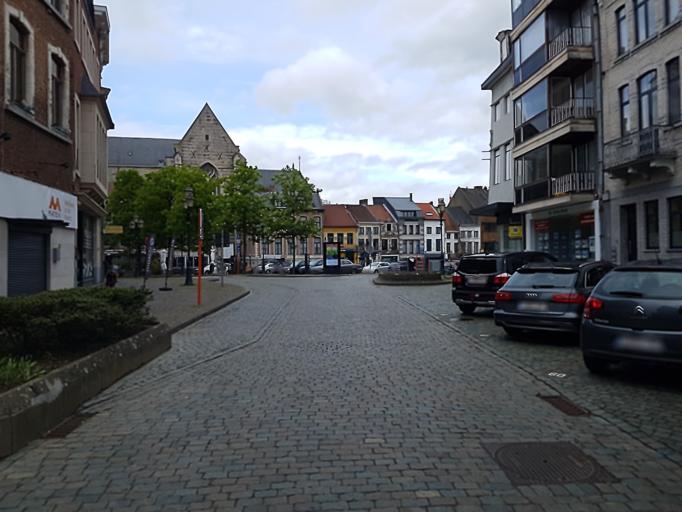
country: BE
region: Flanders
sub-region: Provincie Vlaams-Brabant
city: Tienen
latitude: 50.8048
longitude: 4.9400
